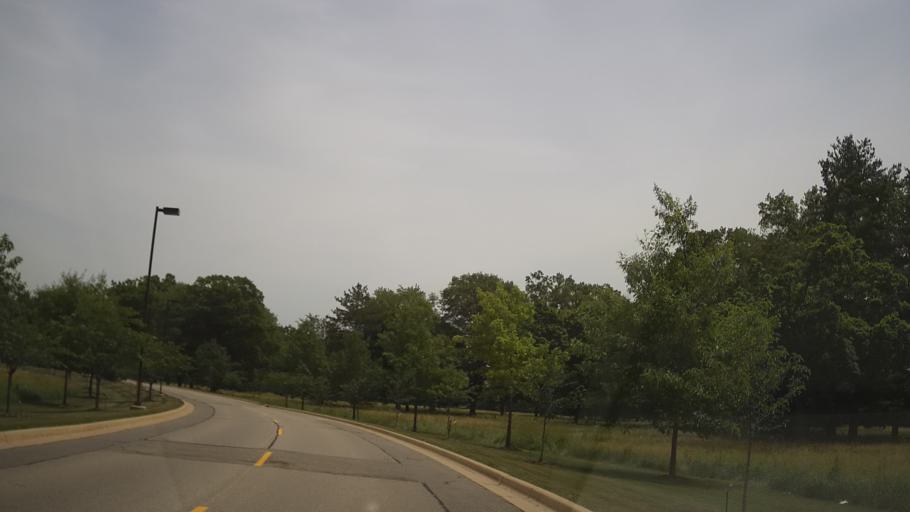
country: US
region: Michigan
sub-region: Washtenaw County
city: Milan
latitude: 42.1588
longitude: -83.6945
